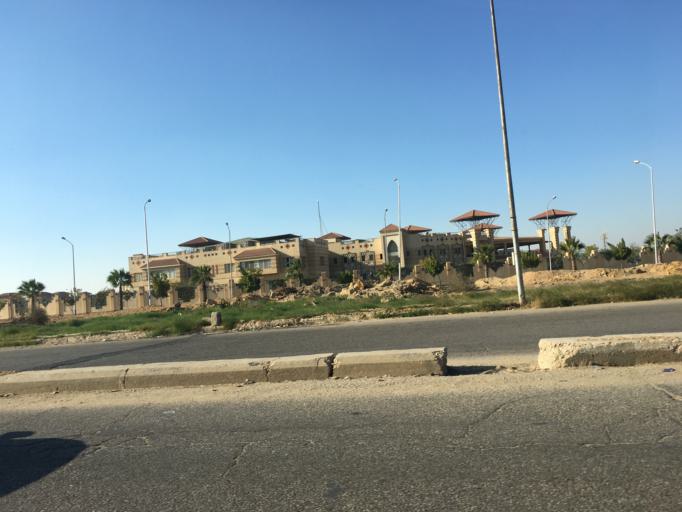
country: EG
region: Al Jizah
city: Madinat Sittah Uktubar
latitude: 29.9961
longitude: 30.9531
